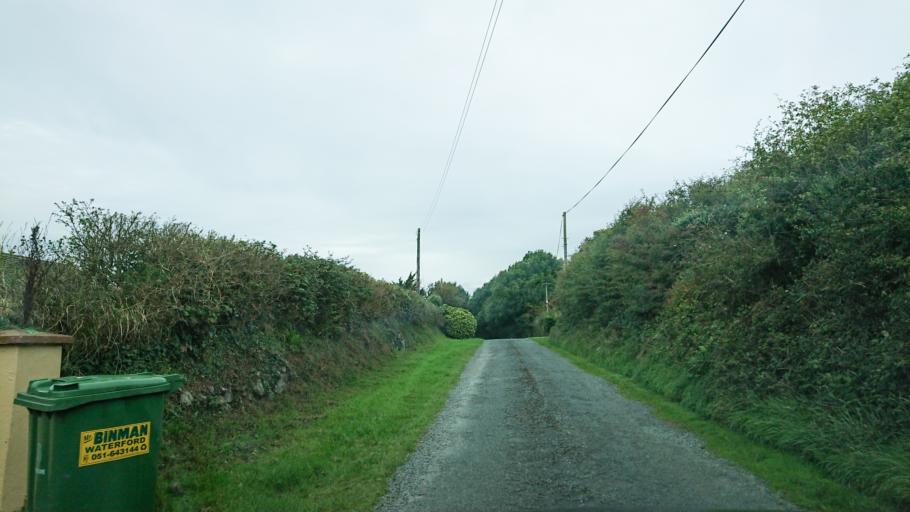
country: IE
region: Munster
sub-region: Waterford
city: Dunmore East
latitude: 52.1970
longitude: -7.0347
